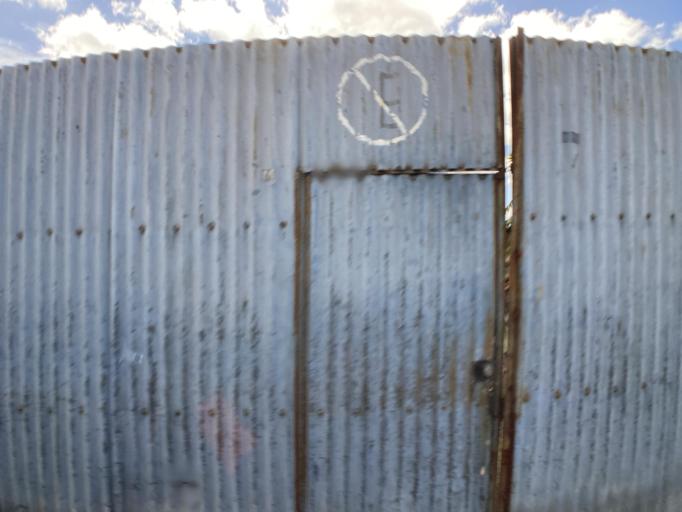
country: GT
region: Sacatepequez
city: Ciudad Vieja
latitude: 14.5257
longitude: -90.7498
